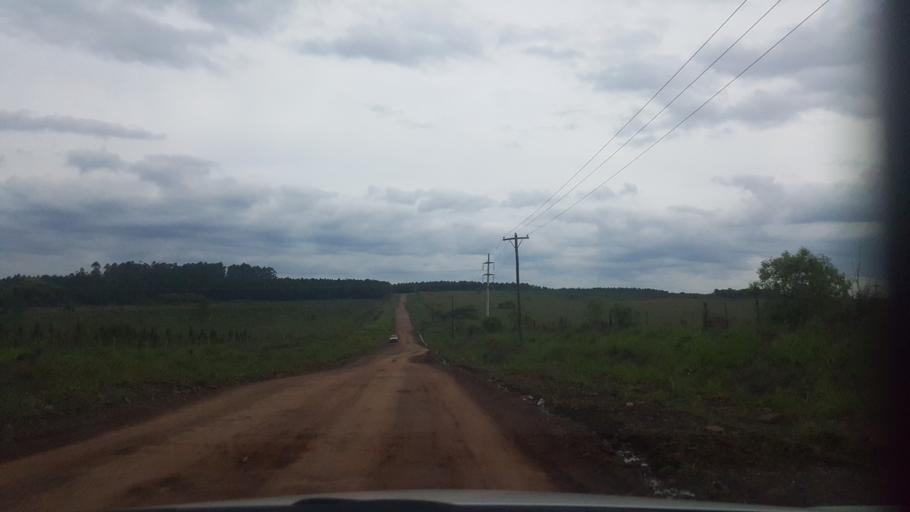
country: AR
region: Misiones
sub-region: Departamento de Candelaria
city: Candelaria
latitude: -27.5027
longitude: -55.7369
